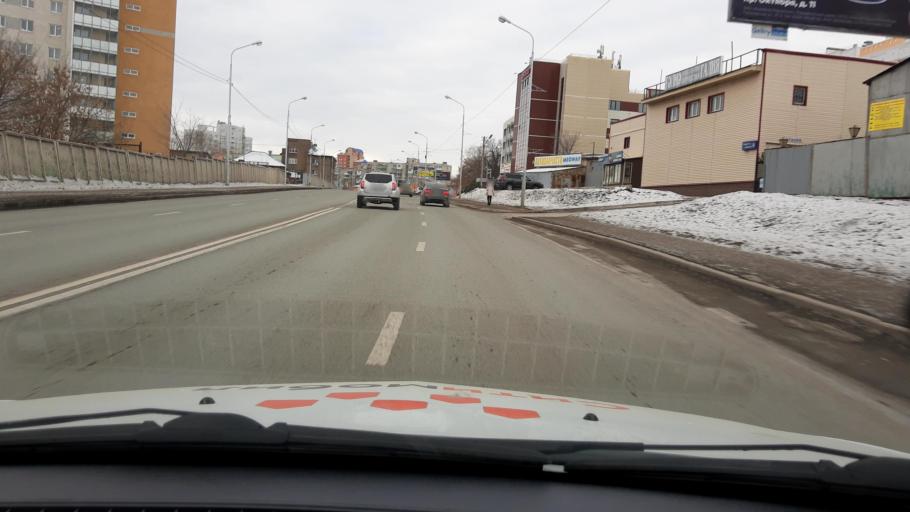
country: RU
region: Bashkortostan
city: Ufa
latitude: 54.7325
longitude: 55.9931
